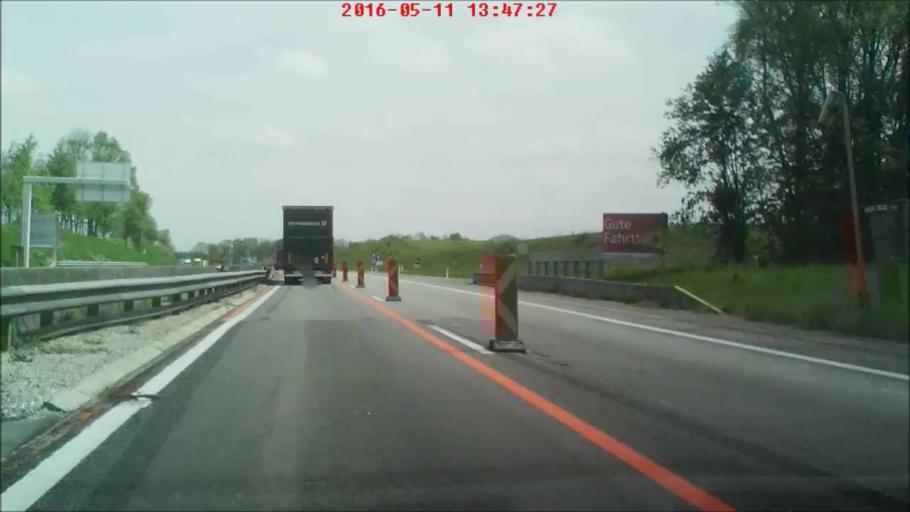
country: AT
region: Upper Austria
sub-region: Politischer Bezirk Vocklabruck
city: Wolfsegg am Hausruck
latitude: 48.1997
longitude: 13.6410
